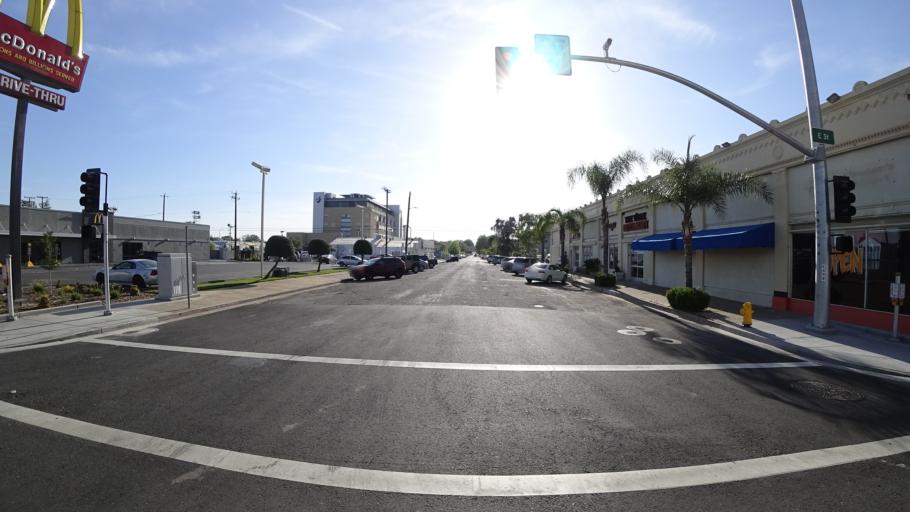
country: US
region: California
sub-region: Yuba County
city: Marysville
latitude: 39.1392
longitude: -121.5905
